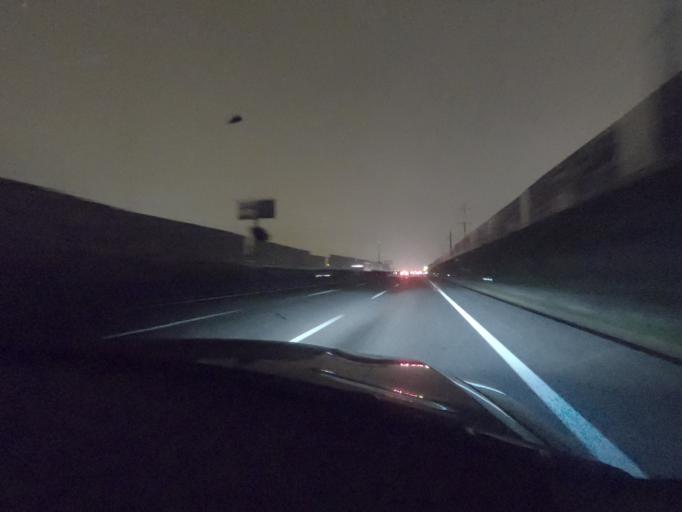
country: PT
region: Lisbon
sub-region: Loures
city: Sao Joao da Talha
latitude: 38.8266
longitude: -9.0985
